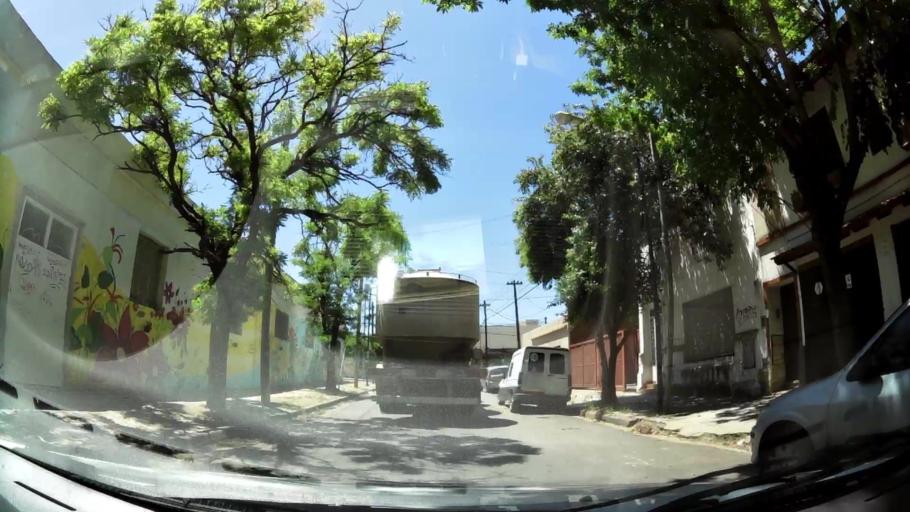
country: AR
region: Buenos Aires
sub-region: Partido de General San Martin
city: General San Martin
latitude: -34.5828
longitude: -58.5434
